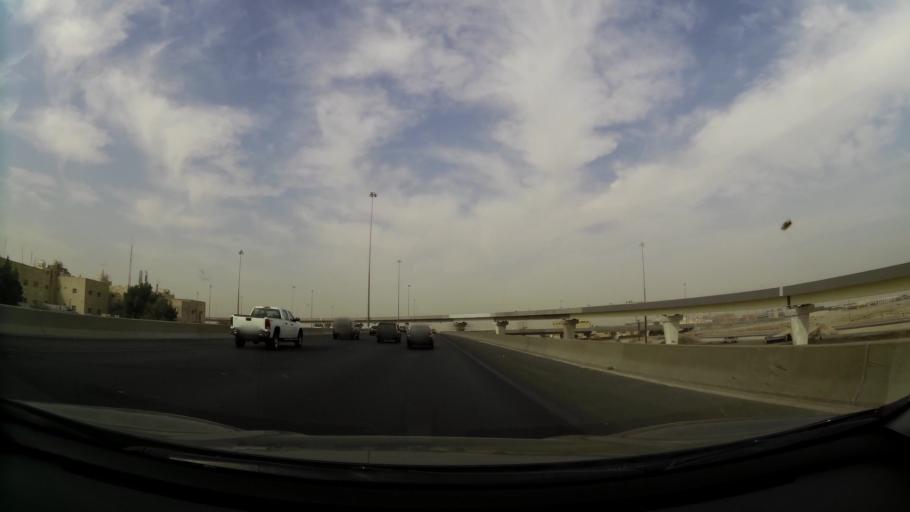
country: KW
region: Al Asimah
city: Ar Rabiyah
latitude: 29.2675
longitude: 47.9113
